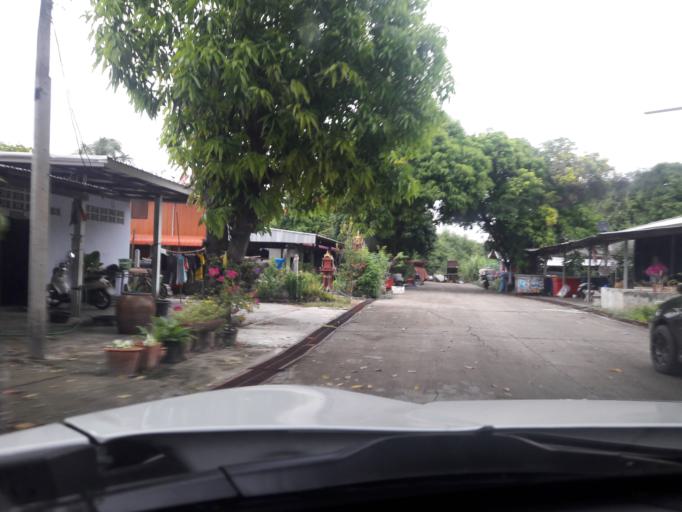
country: TH
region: Lop Buri
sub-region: Amphoe Tha Luang
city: Tha Luang
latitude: 15.0683
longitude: 101.1117
